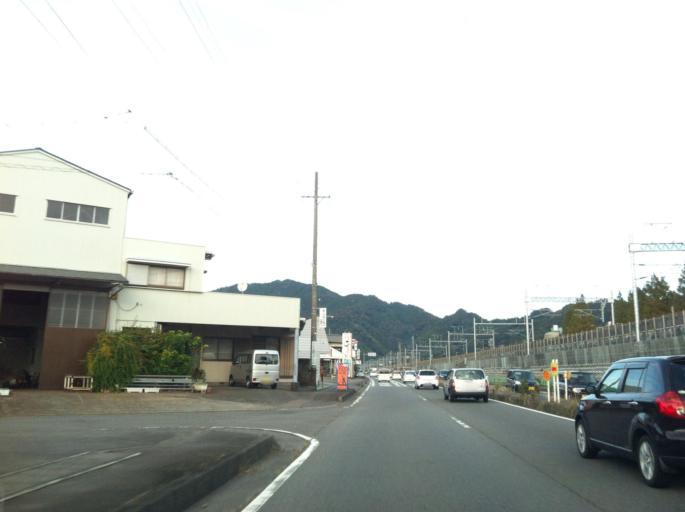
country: JP
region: Shizuoka
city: Yaizu
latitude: 34.8840
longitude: 138.3223
